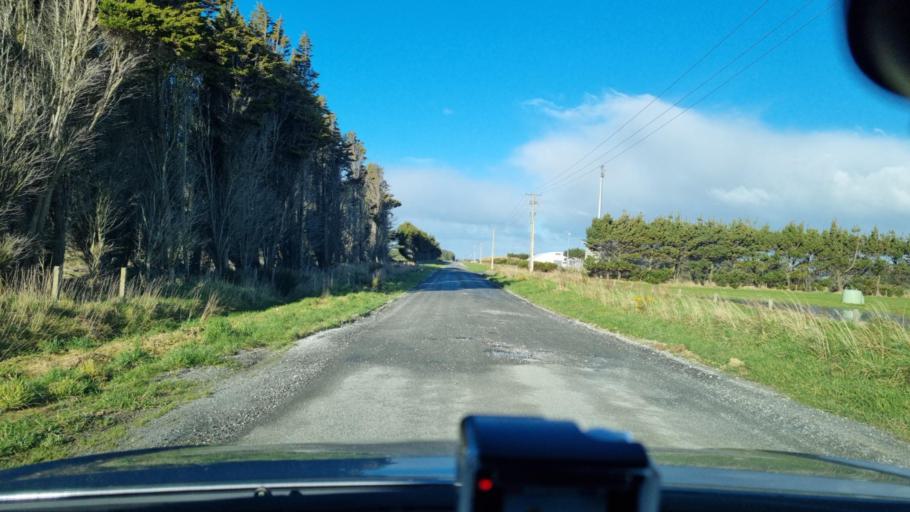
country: NZ
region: Southland
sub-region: Invercargill City
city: Invercargill
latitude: -46.4939
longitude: 168.3836
